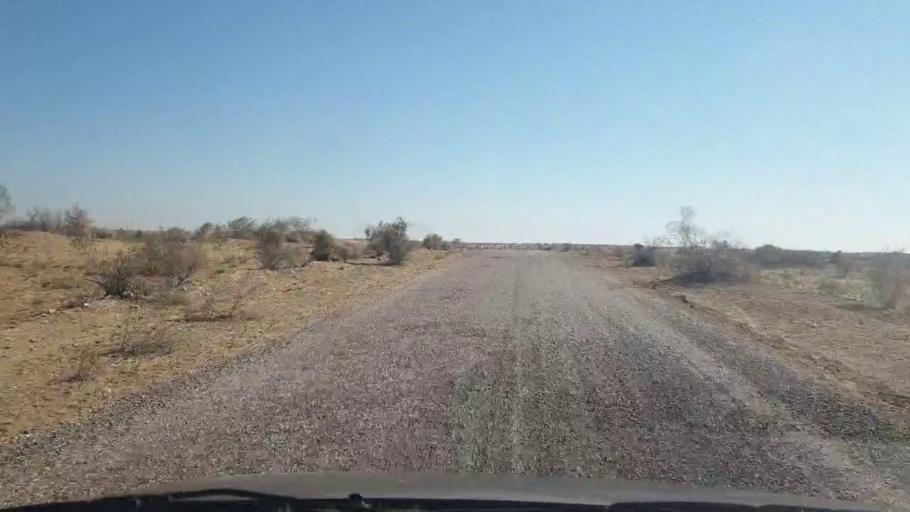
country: PK
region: Sindh
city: Bozdar
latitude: 27.0017
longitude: 68.8079
